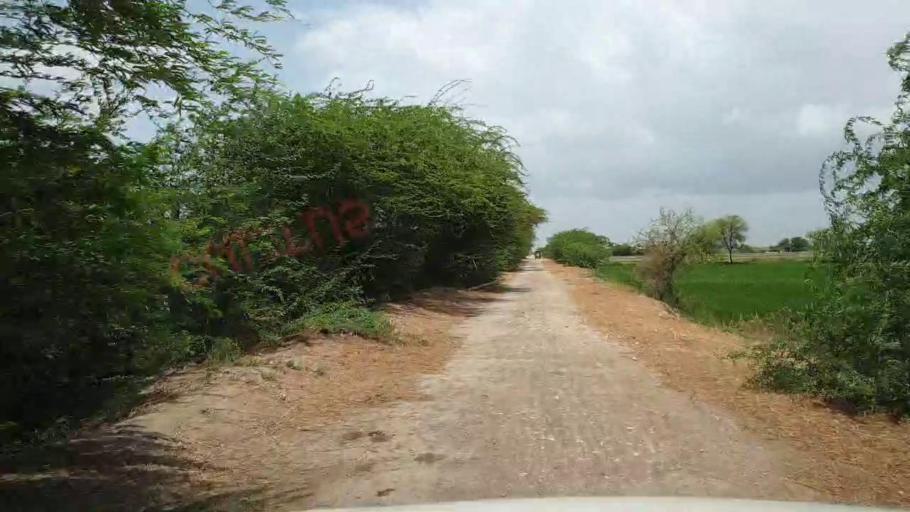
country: PK
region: Sindh
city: Kario
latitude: 24.6971
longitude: 68.6399
